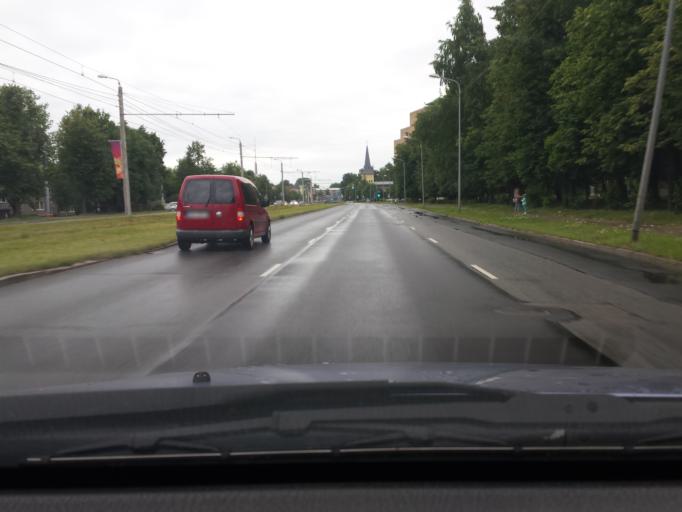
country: LV
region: Kekava
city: Balozi
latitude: 56.9071
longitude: 24.1871
